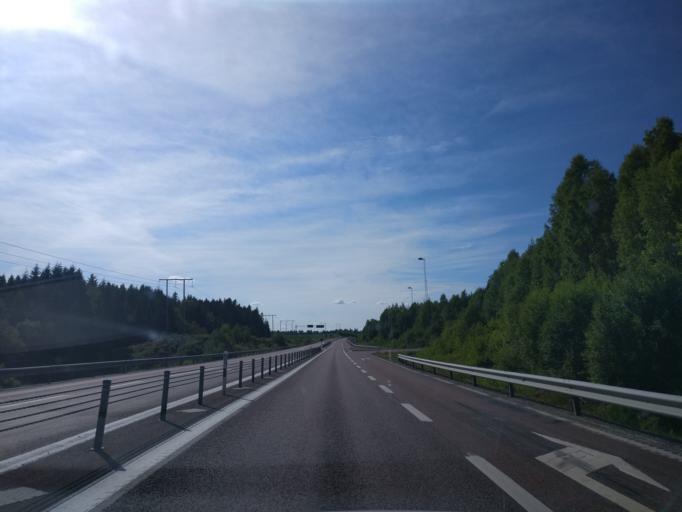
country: SE
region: Vaermland
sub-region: Kils Kommun
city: Kil
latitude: 59.4985
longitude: 13.2797
